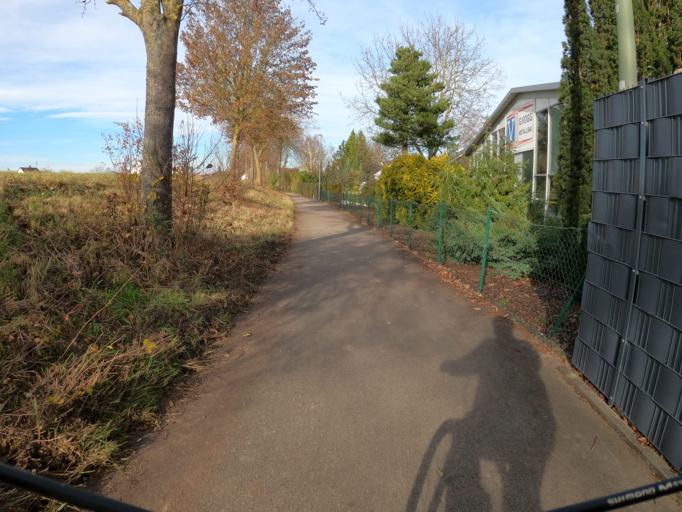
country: DE
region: Bavaria
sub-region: Swabia
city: Leipheim
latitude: 48.4145
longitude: 10.1921
